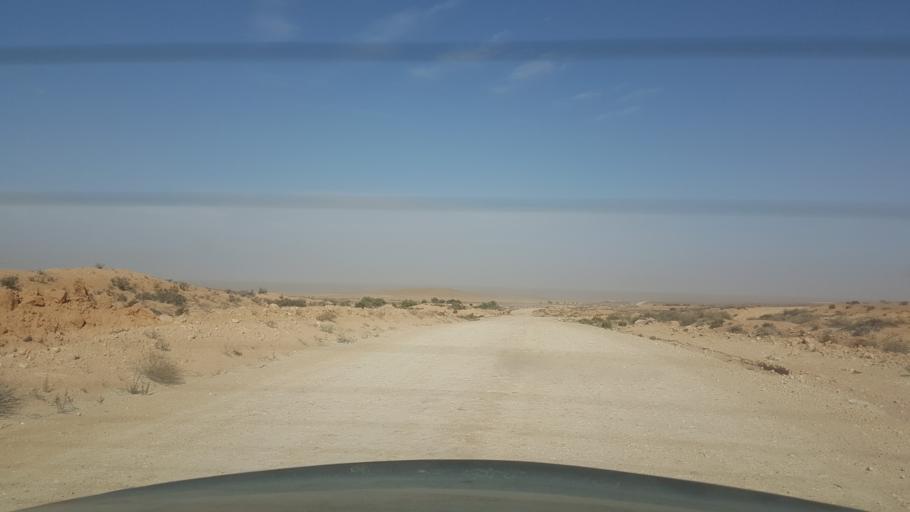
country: TN
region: Qabis
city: El Hamma
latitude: 33.6609
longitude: 9.7348
